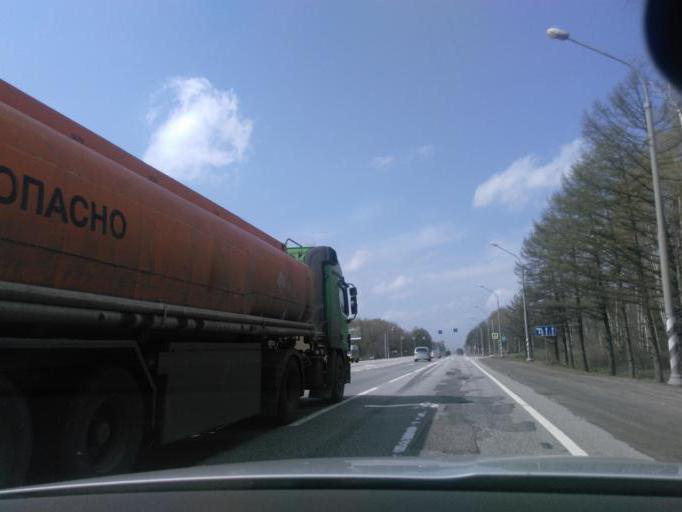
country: RU
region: Moskovskaya
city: Chashnikovo
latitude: 56.0230
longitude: 37.1859
